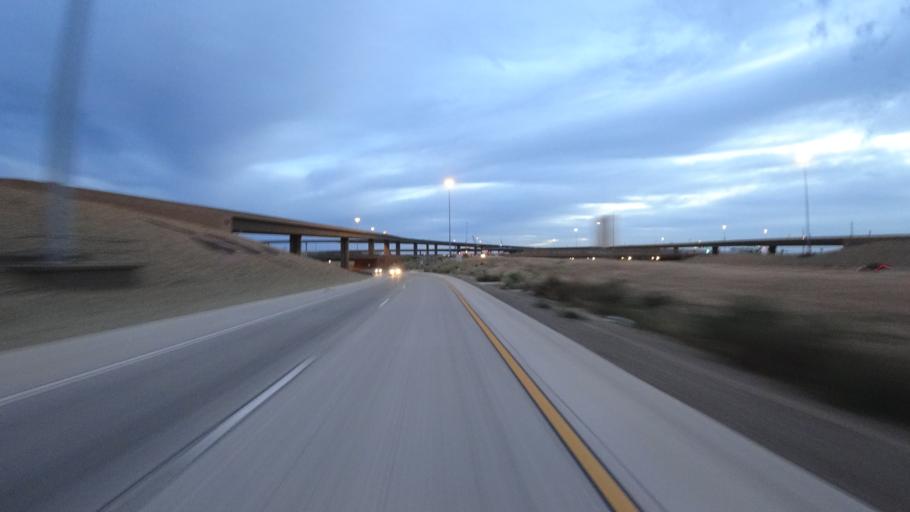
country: US
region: Arizona
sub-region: Maricopa County
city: Litchfield Park
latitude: 33.4667
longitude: -112.4264
